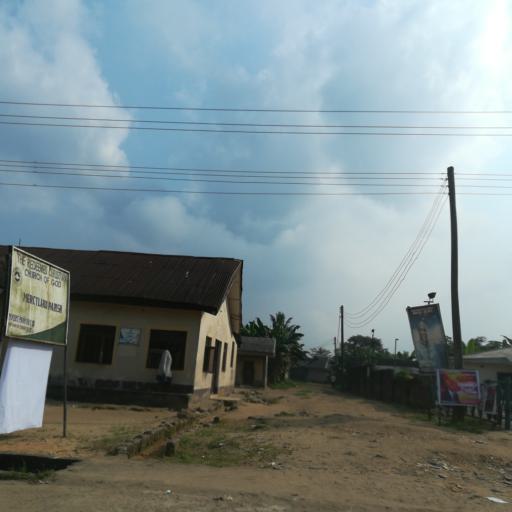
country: NG
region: Rivers
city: Okrika
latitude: 4.7771
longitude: 7.1571
